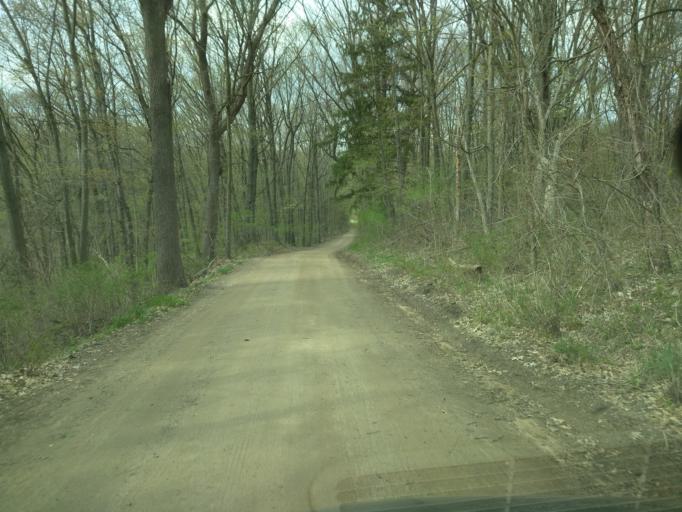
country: US
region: Michigan
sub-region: Eaton County
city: Waverly
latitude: 42.6932
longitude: -84.6227
